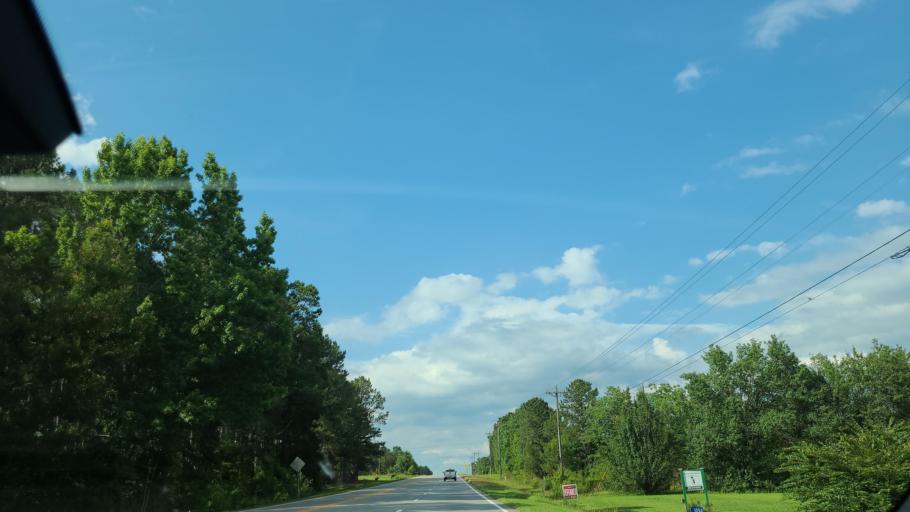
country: US
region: Georgia
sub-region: Jones County
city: Gray
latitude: 33.0688
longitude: -83.4880
